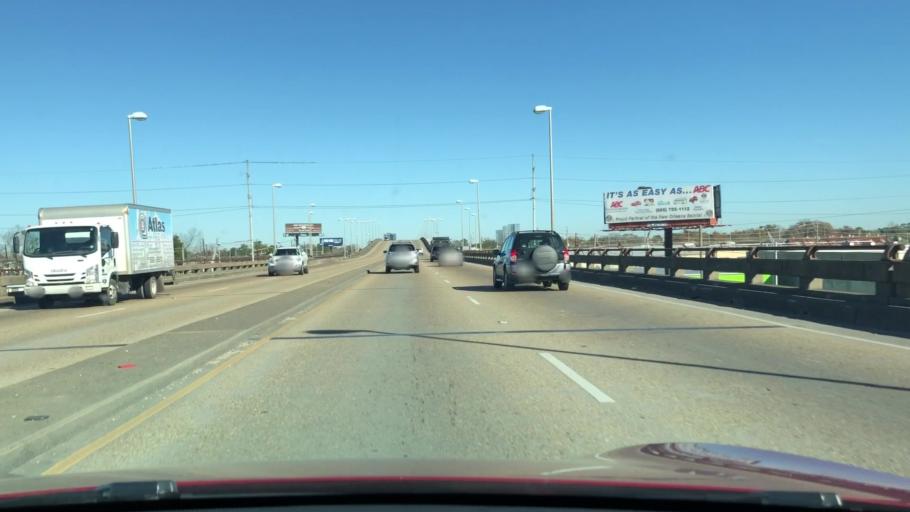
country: US
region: Louisiana
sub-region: Jefferson Parish
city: Jefferson
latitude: 29.9710
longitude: -90.1565
